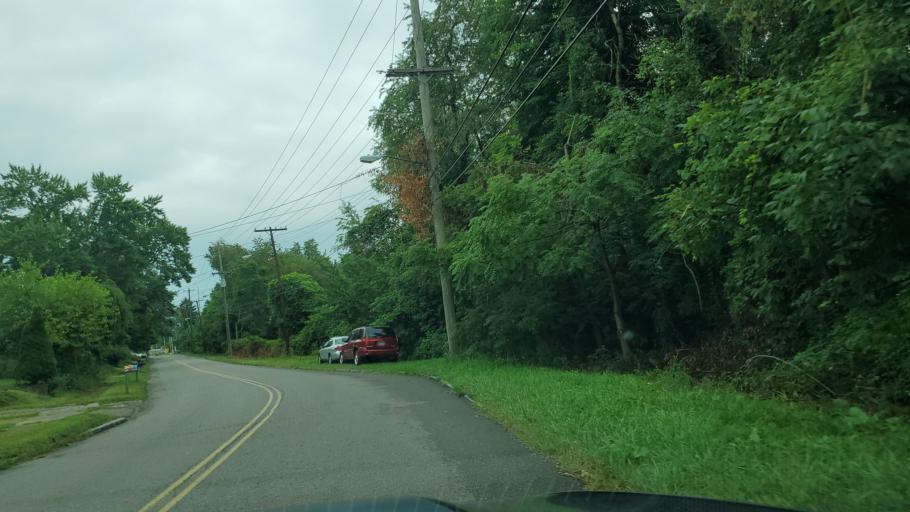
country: US
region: Ohio
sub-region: Trumbull County
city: McDonald
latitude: 41.1712
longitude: -80.7452
